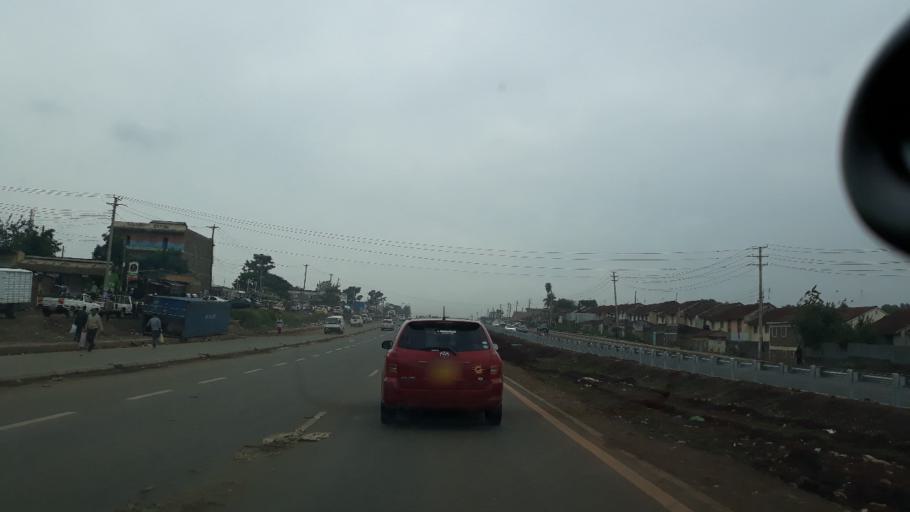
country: KE
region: Nairobi Area
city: Pumwani
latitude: -1.2654
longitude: 36.8796
